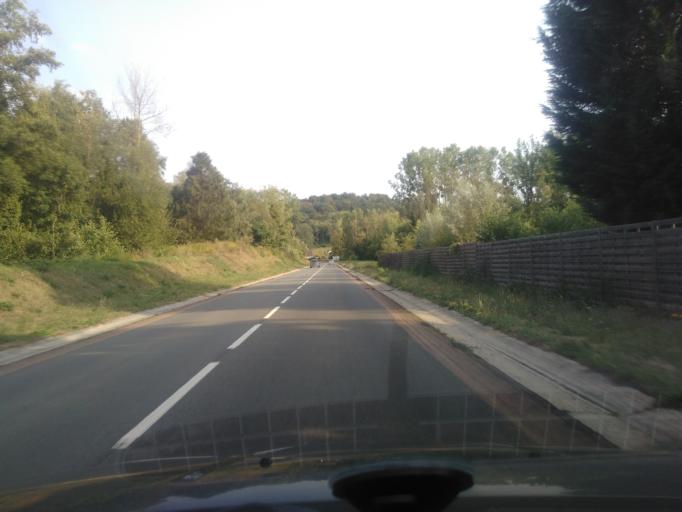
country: FR
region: Picardie
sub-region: Departement de l'Aisne
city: Bruyeres-et-Montberault
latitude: 49.5275
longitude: 3.6548
